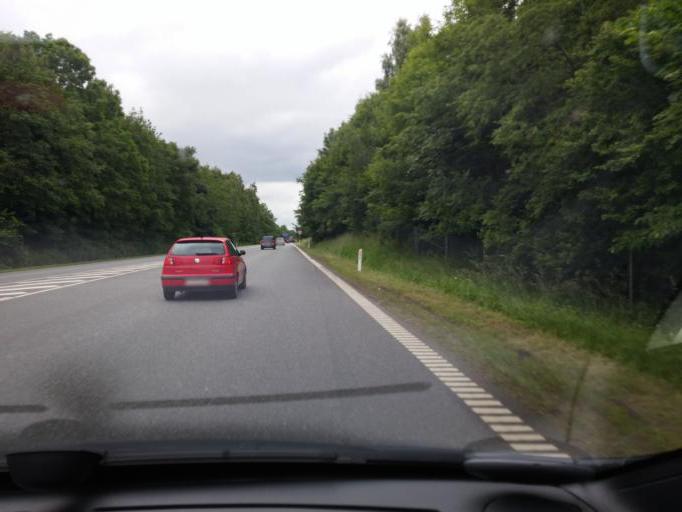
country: DK
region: Capital Region
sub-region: Hillerod Kommune
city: Nodebo
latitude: 55.9374
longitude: 12.3572
